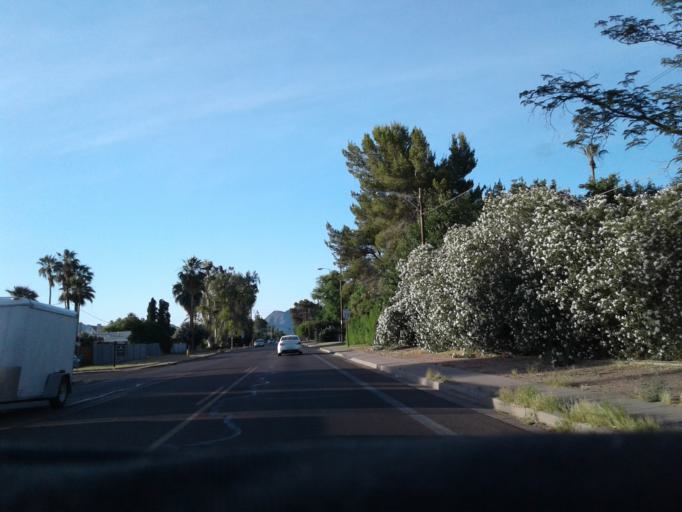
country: US
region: Arizona
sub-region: Maricopa County
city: Paradise Valley
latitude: 33.4848
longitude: -111.9955
